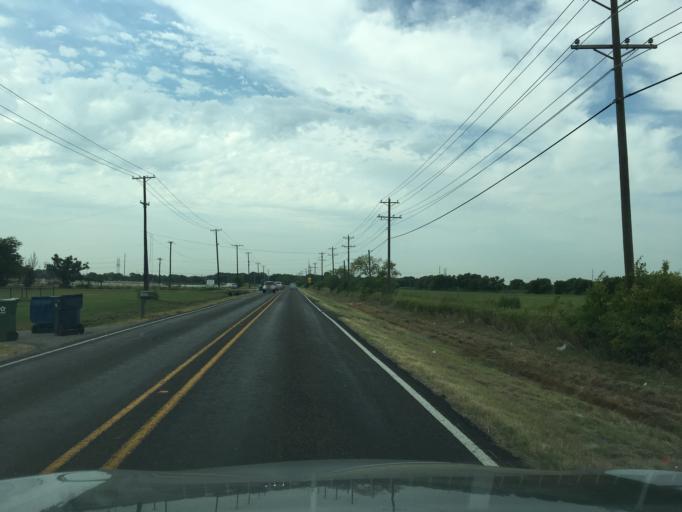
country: US
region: Texas
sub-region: Collin County
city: Parker
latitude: 33.0699
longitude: -96.6204
